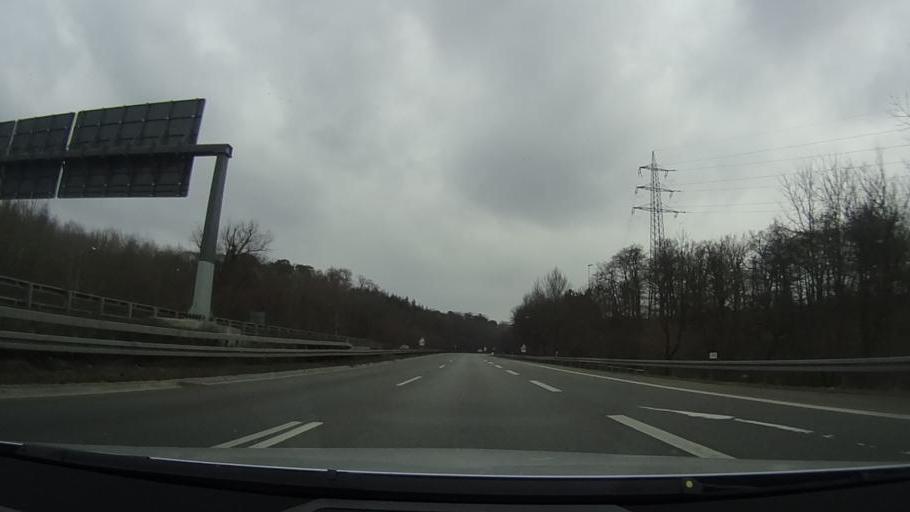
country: DE
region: Hesse
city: Kelsterbach
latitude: 50.0699
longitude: 8.5457
